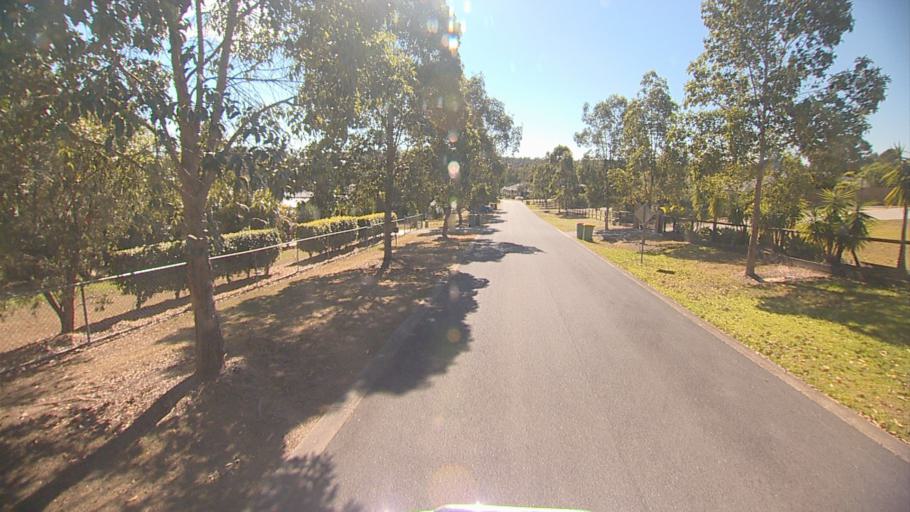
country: AU
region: Queensland
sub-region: Logan
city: North Maclean
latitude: -27.7597
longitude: 152.9520
